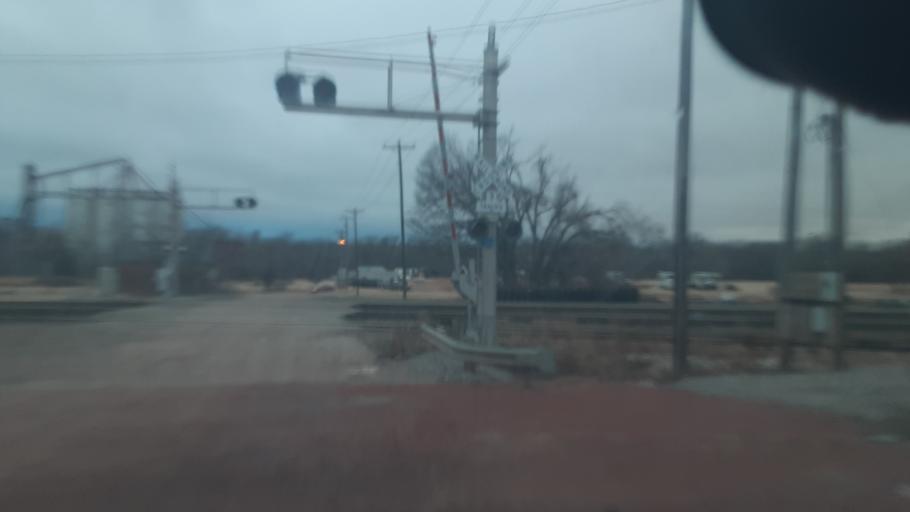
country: US
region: Oklahoma
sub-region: Logan County
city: Guthrie
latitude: 35.8760
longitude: -97.4302
